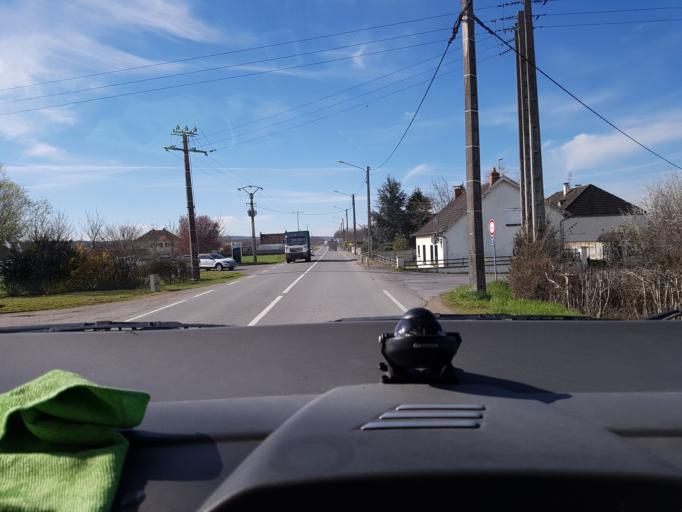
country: FR
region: Bourgogne
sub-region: Departement de Saone-et-Loire
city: Gueugnon
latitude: 46.5892
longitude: 4.0647
